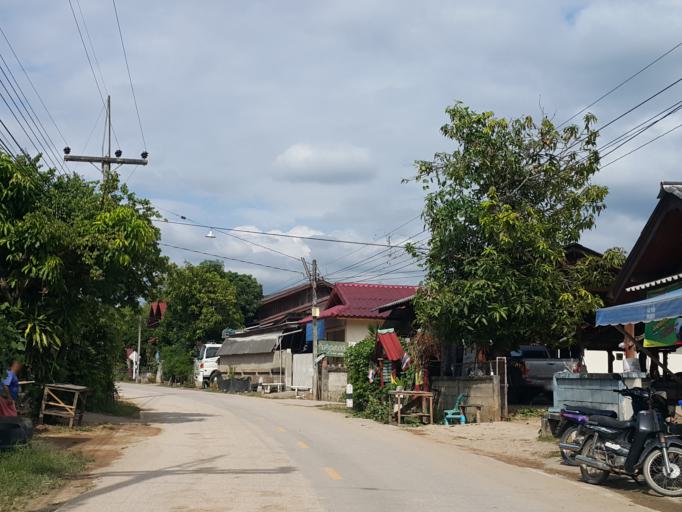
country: TH
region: Lampang
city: Chae Hom
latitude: 18.5635
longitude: 99.4590
